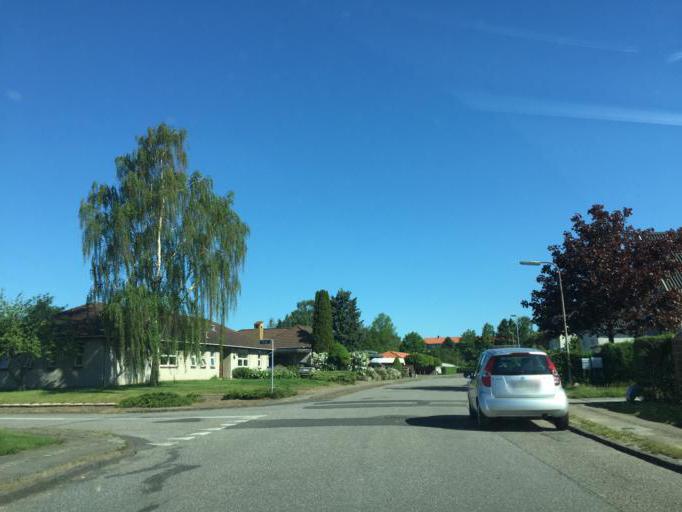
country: DK
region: South Denmark
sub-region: Odense Kommune
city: Odense
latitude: 55.3552
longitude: 10.3867
